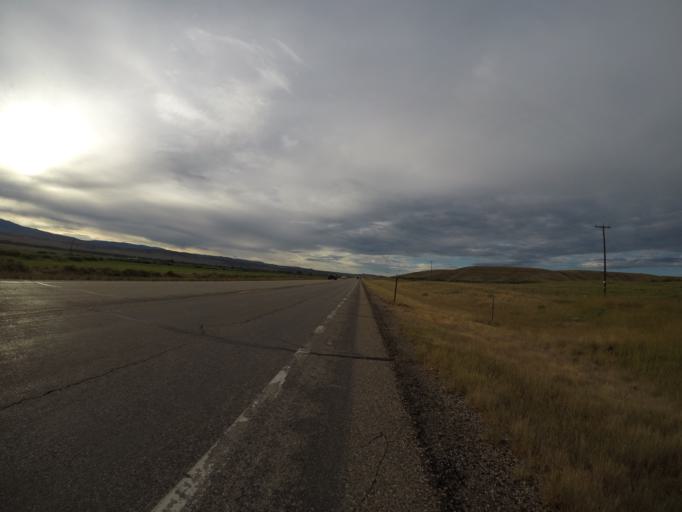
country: US
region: Wyoming
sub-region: Carbon County
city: Saratoga
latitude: 41.3915
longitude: -106.7590
